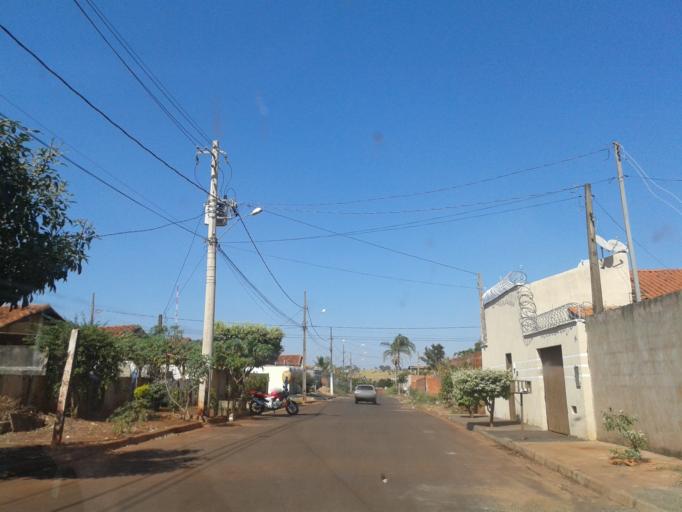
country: BR
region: Minas Gerais
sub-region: Ituiutaba
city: Ituiutaba
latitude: -18.9937
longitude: -49.4605
